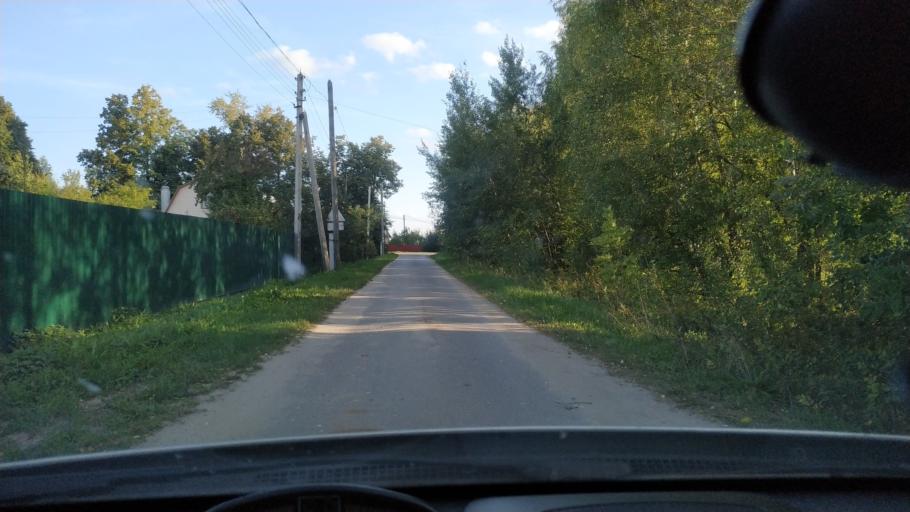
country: RU
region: Rjazan
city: Solotcha
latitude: 54.8672
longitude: 39.6697
